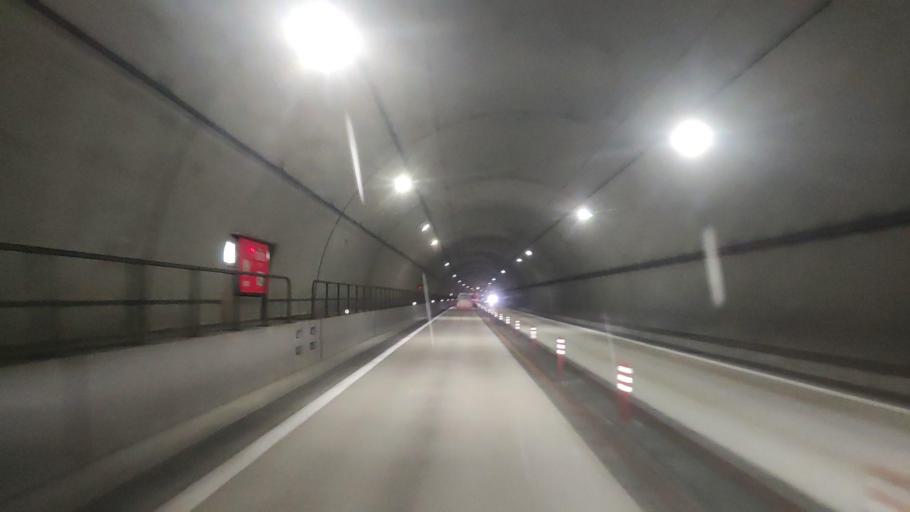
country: JP
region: Wakayama
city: Tanabe
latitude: 33.5874
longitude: 135.4447
